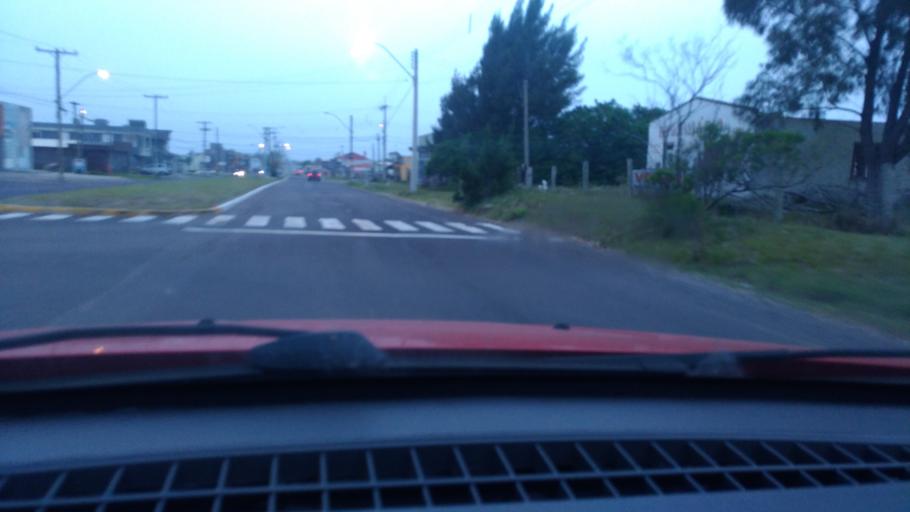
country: BR
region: Rio Grande do Sul
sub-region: Capao Da Canoa
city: Capao da Canoa
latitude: -29.8503
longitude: -50.0736
